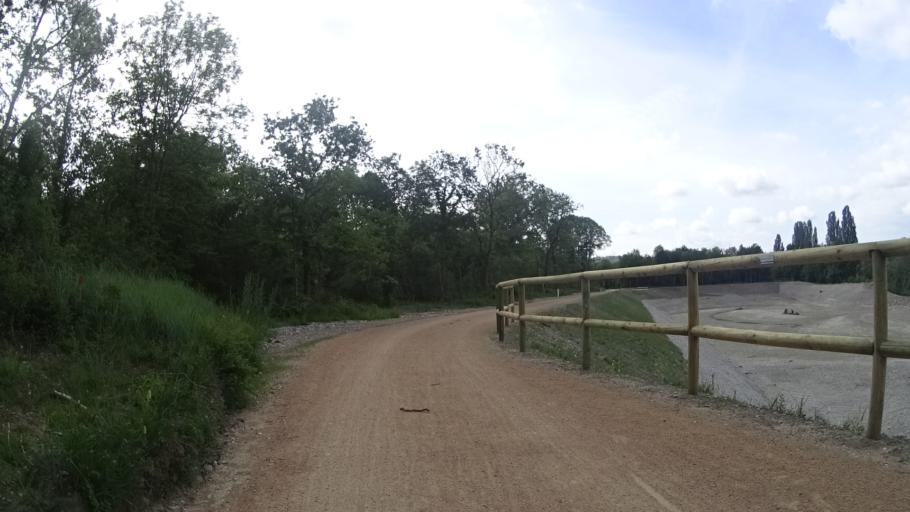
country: DE
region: Baden-Wuerttemberg
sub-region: Freiburg Region
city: Bad Bellingen
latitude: 47.7469
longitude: 7.5468
